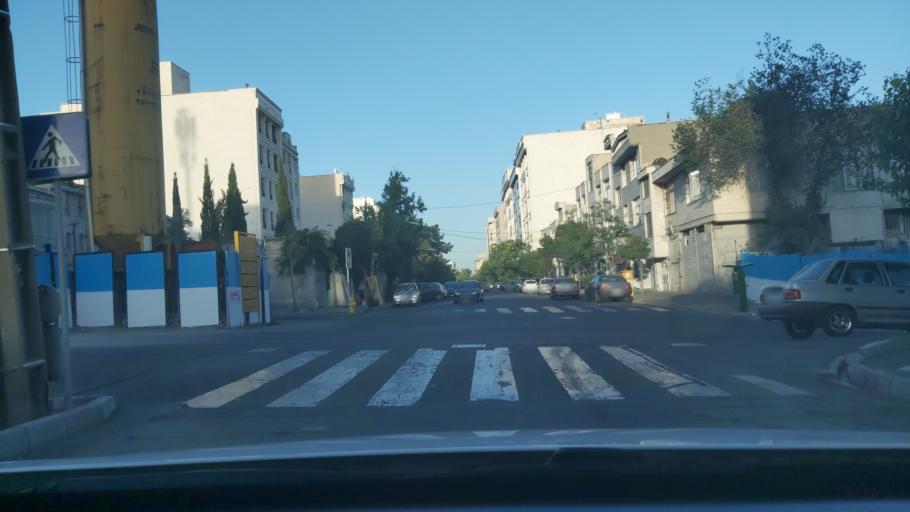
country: IR
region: Tehran
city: Tehran
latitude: 35.7312
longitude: 51.3071
